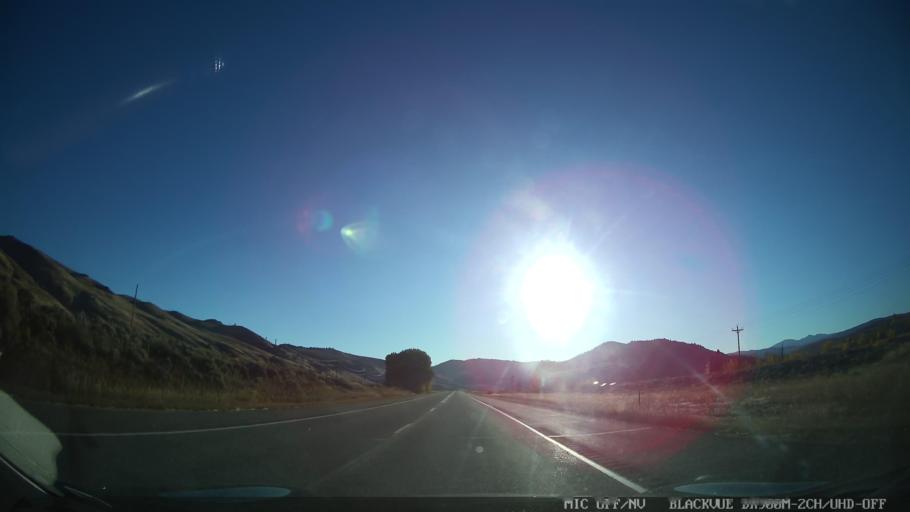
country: US
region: Colorado
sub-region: Grand County
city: Hot Sulphur Springs
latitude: 40.0518
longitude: -106.1562
